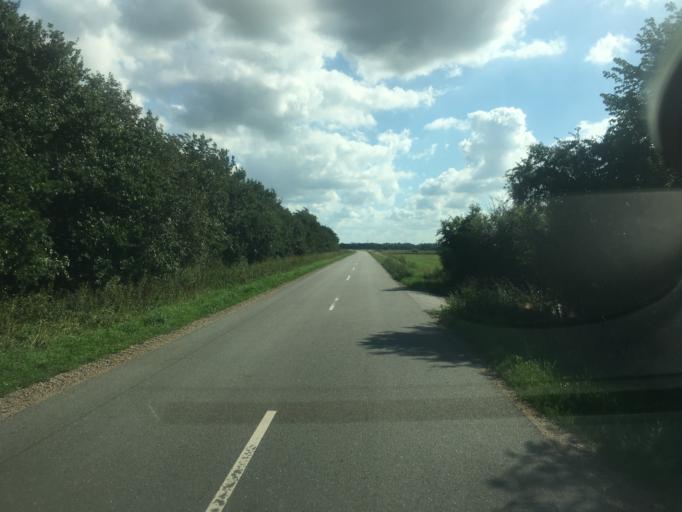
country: DE
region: Schleswig-Holstein
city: Ellhoft
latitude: 54.9592
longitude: 8.9608
